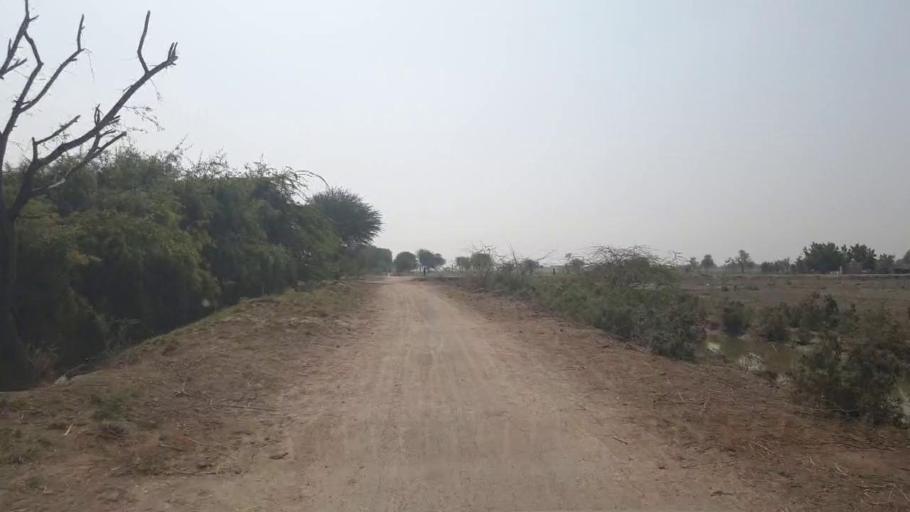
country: PK
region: Sindh
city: Dhoro Naro
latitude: 25.4388
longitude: 69.6263
